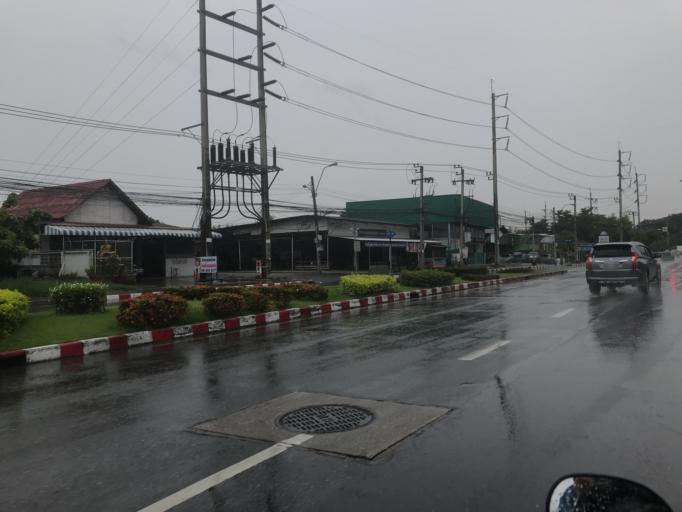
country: TH
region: Bangkok
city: Bueng Kum
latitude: 13.7906
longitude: 100.6805
